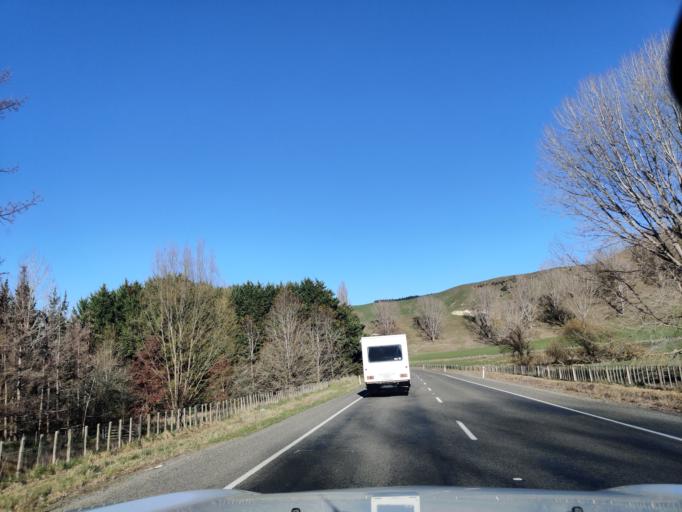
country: NZ
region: Manawatu-Wanganui
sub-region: Ruapehu District
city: Waiouru
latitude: -39.7413
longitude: 175.8380
